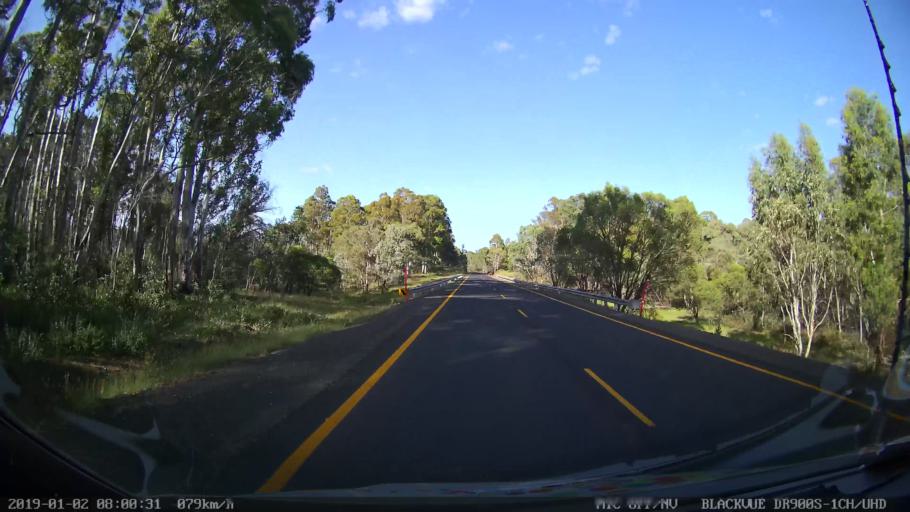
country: AU
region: New South Wales
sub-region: Tumut Shire
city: Tumut
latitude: -35.6447
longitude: 148.4443
